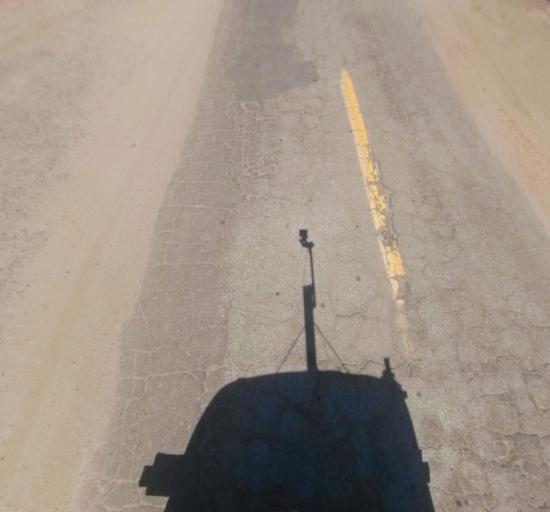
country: US
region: California
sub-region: Madera County
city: Chowchilla
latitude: 37.0327
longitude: -120.3067
